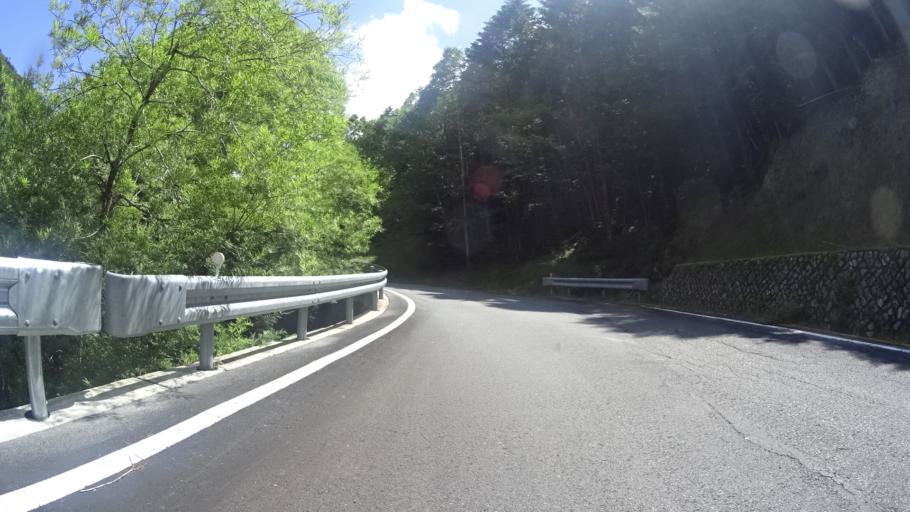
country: JP
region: Yamanashi
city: Enzan
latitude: 35.8596
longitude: 138.6565
